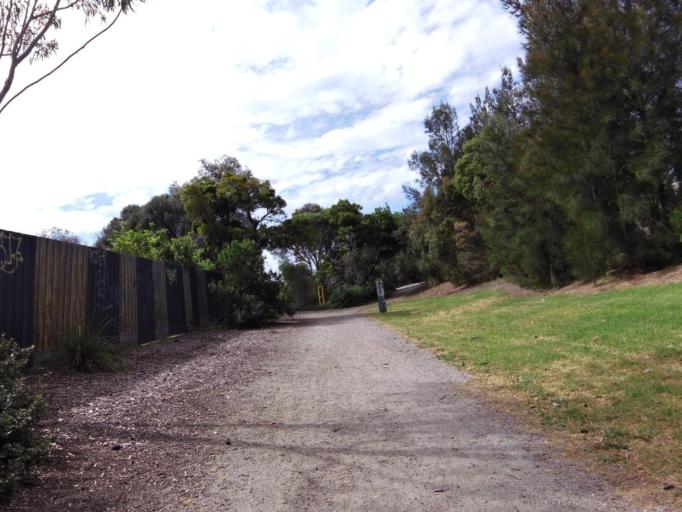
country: AU
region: Victoria
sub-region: Kingston
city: Carrum
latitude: -38.0798
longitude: 145.1337
